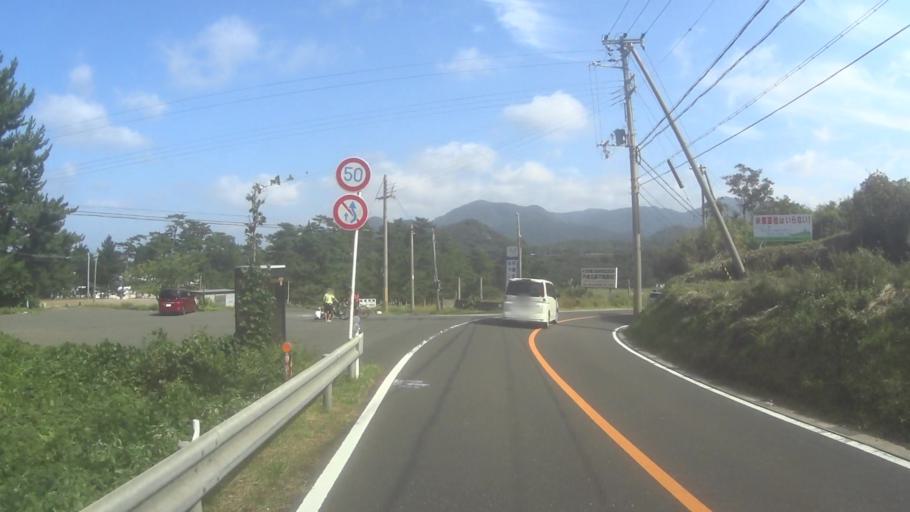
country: JP
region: Kyoto
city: Miyazu
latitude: 35.7517
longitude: 135.1576
